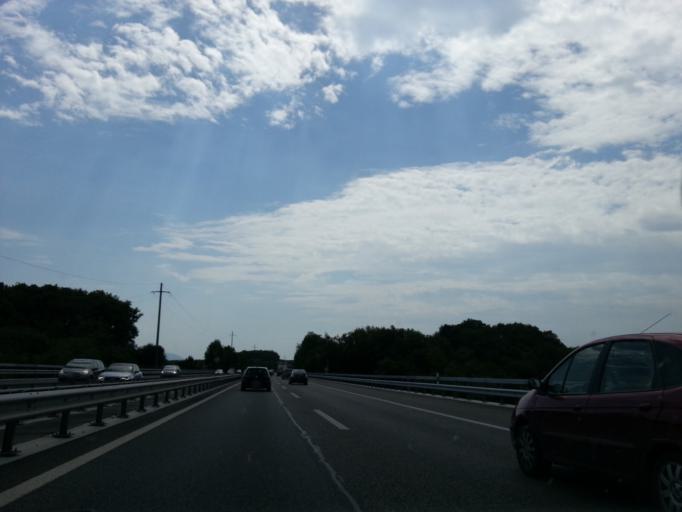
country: CH
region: Geneva
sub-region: Geneva
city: Versoix
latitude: 46.2812
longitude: 6.1436
